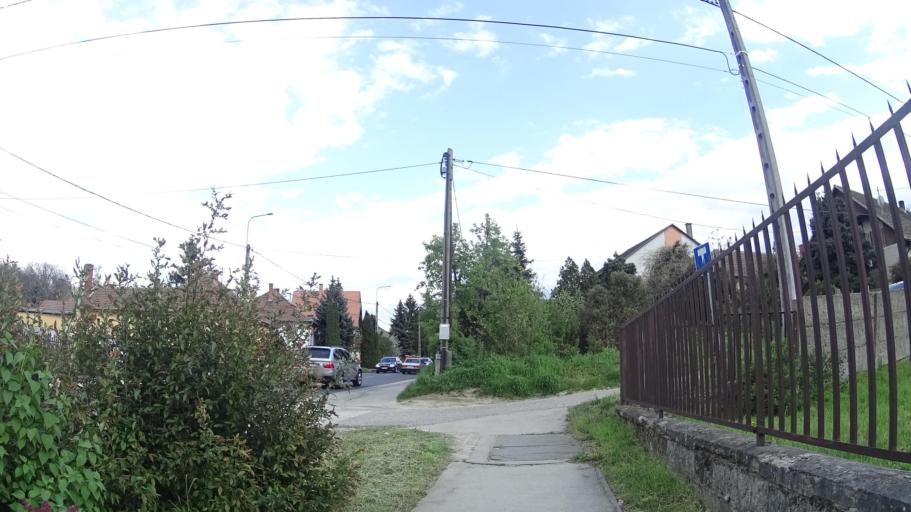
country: HU
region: Pest
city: Szada
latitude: 47.6315
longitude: 19.3179
